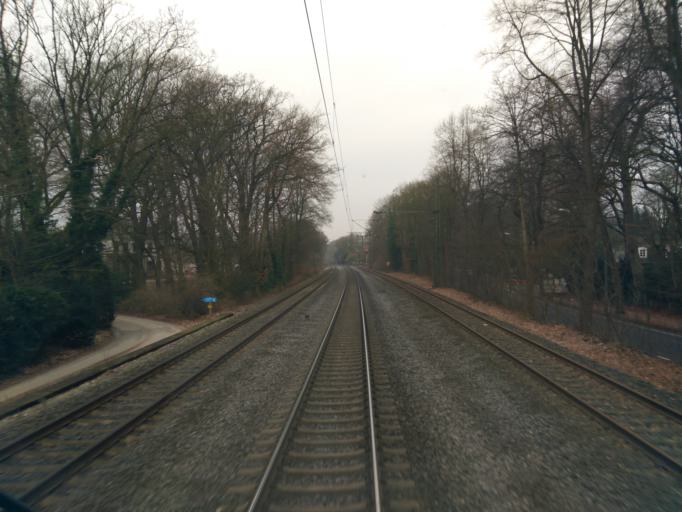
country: DE
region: Lower Saxony
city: Lilienthal
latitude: 53.0896
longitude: 8.9282
